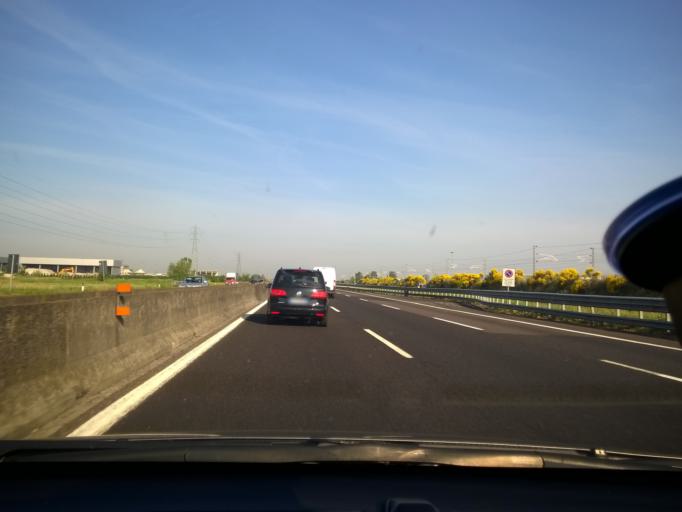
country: IT
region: Emilia-Romagna
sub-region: Provincia di Reggio Emilia
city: Prato
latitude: 44.7075
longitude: 10.7295
